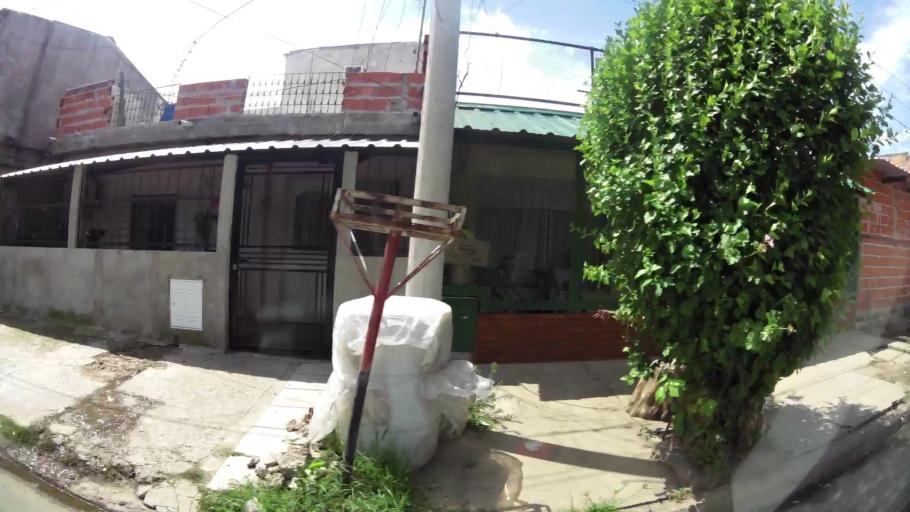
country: AR
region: Santa Fe
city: Gobernador Galvez
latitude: -33.0071
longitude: -60.6433
